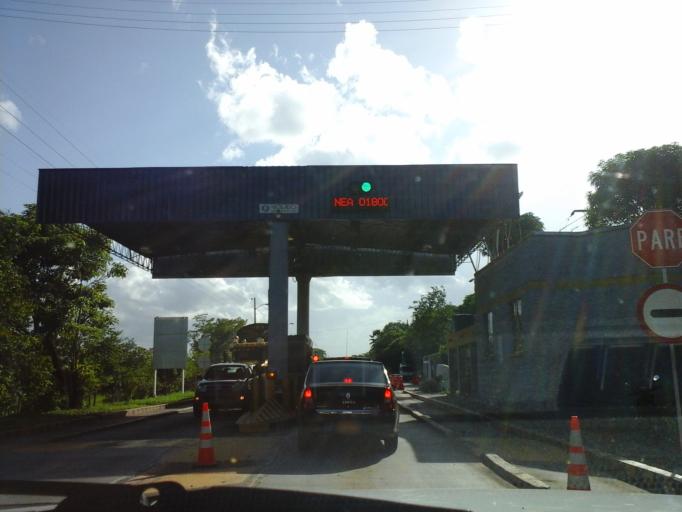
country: CO
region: Meta
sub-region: Villavicencio
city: Villavicencio
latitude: 4.0570
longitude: -73.4630
